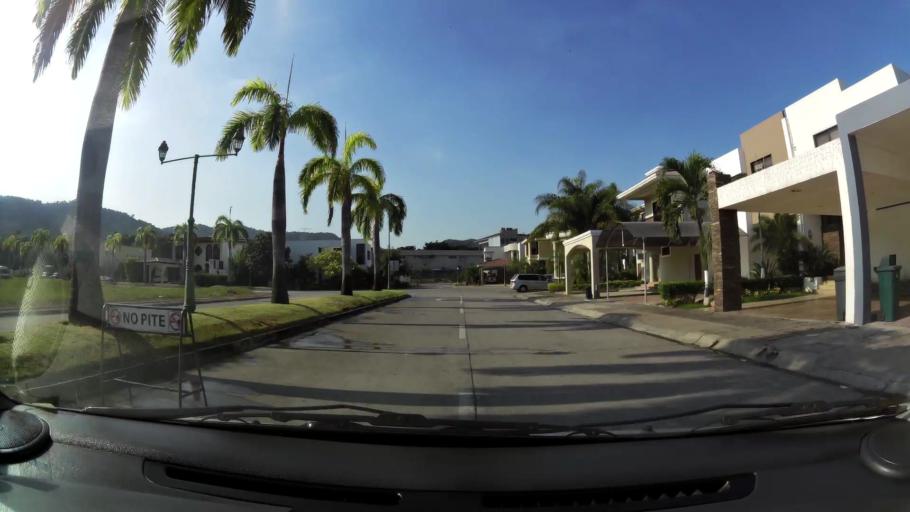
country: EC
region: Guayas
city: Santa Lucia
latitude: -2.1853
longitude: -79.9840
